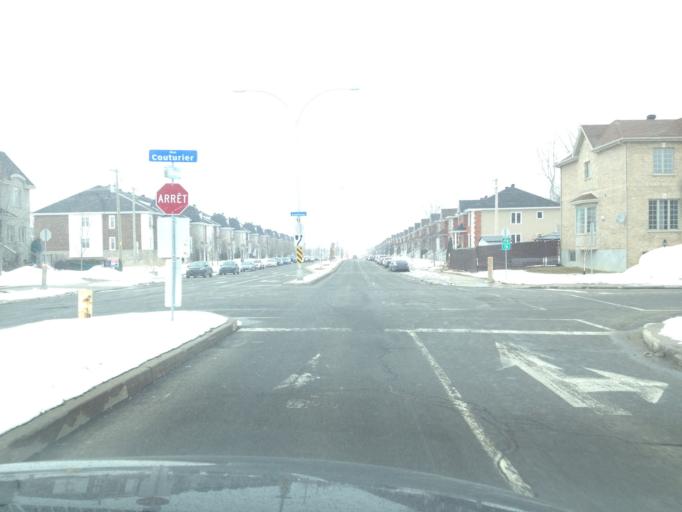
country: CA
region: Quebec
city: Dollard-Des Ormeaux
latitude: 45.5510
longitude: -73.7824
